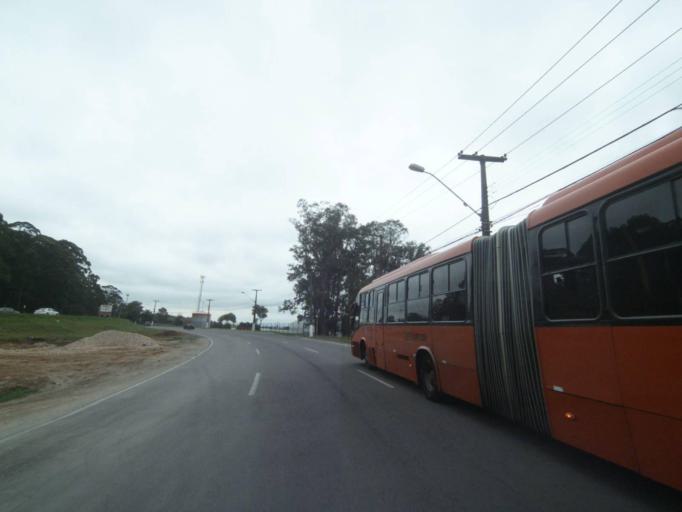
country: BR
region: Parana
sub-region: Sao Jose Dos Pinhais
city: Sao Jose dos Pinhais
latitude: -25.5381
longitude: -49.3102
